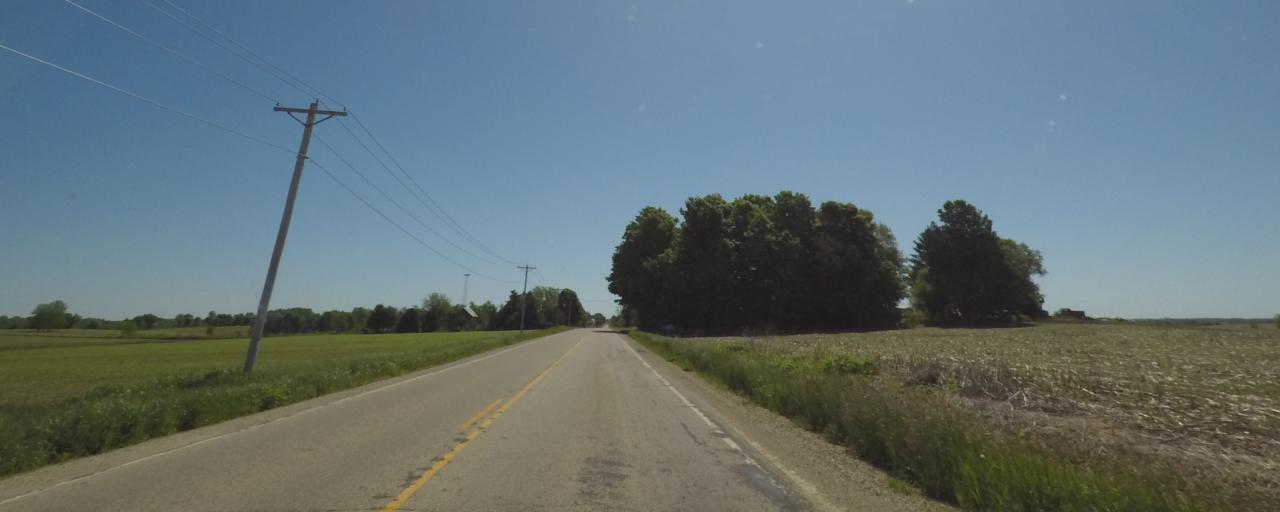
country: US
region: Wisconsin
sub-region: Rock County
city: Evansville
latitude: 42.7876
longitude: -89.3384
